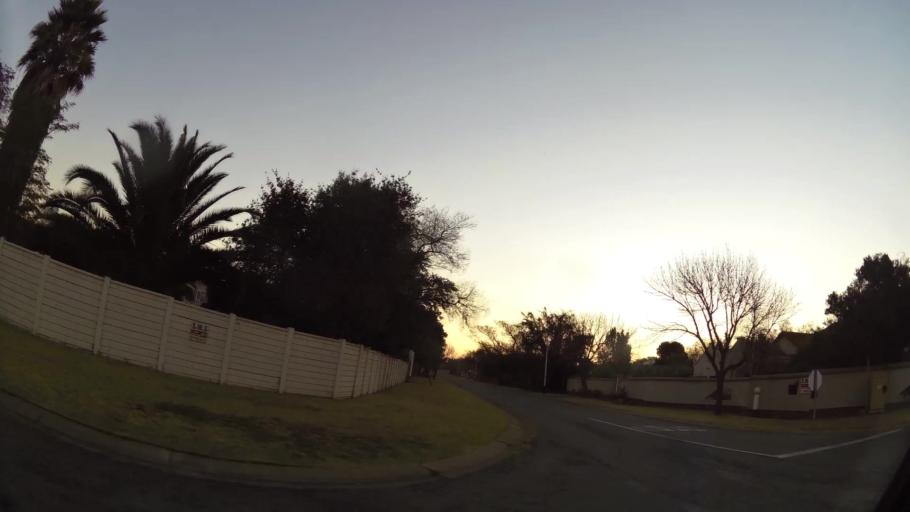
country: ZA
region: Gauteng
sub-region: Ekurhuleni Metropolitan Municipality
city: Germiston
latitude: -26.2600
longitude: 28.1546
